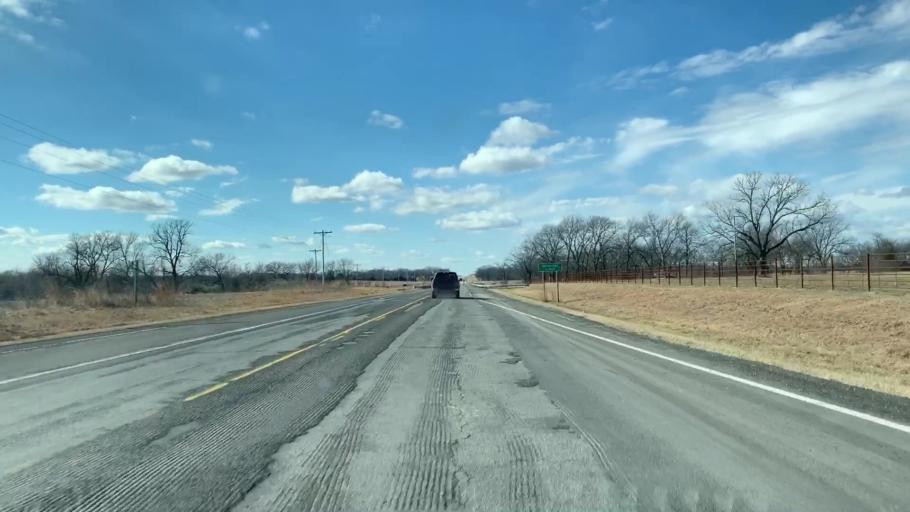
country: US
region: Kansas
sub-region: Labette County
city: Parsons
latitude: 37.3404
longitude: -95.1319
